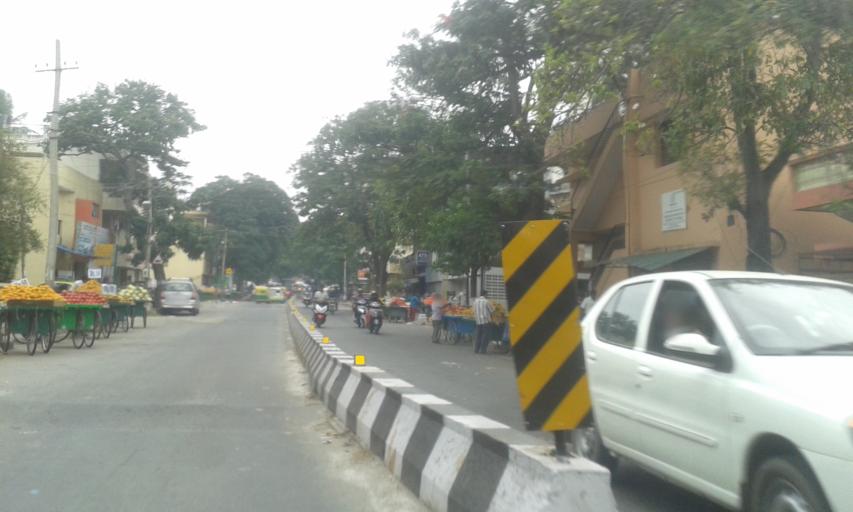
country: IN
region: Karnataka
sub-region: Bangalore Urban
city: Bangalore
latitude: 12.9205
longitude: 77.5985
